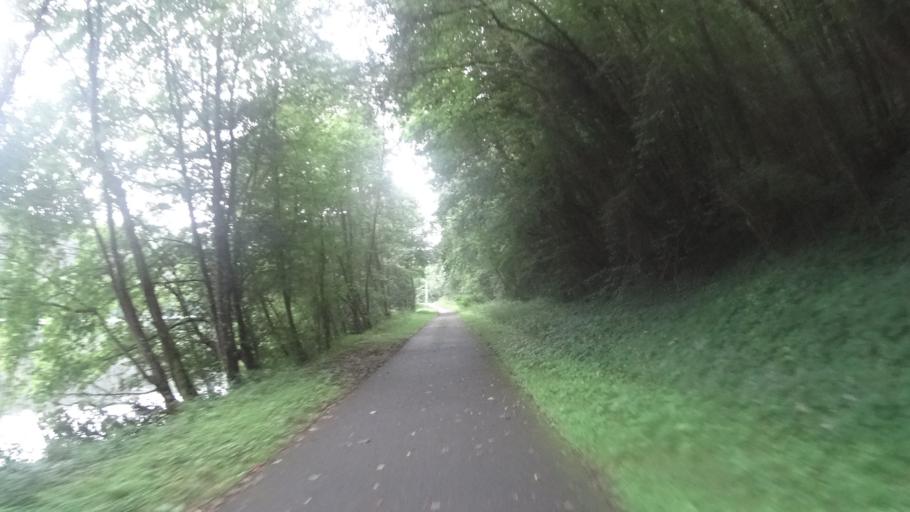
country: FR
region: Lorraine
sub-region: Departement de Meurthe-et-Moselle
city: Velaine-en-Haye
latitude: 48.6548
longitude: 6.0300
